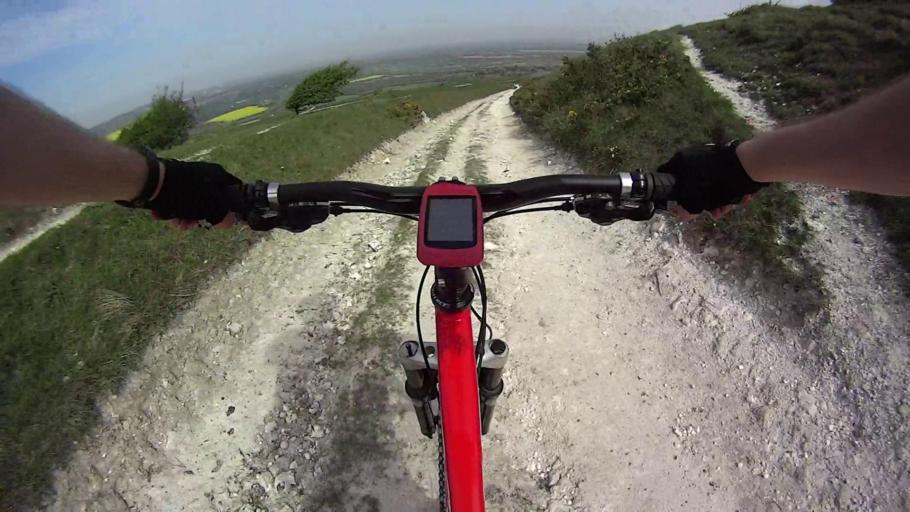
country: GB
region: England
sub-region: East Sussex
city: Seaford
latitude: 50.8079
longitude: 0.1853
